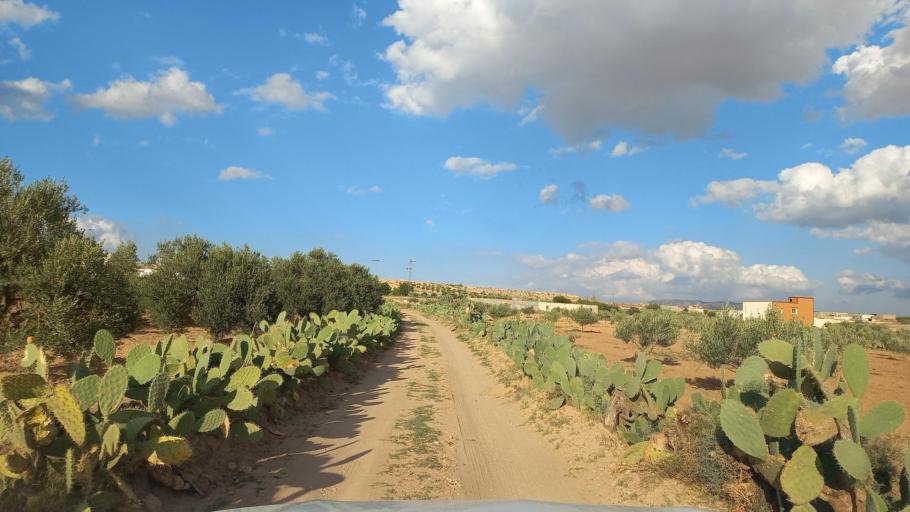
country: TN
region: Al Qasrayn
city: Sbiba
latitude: 35.3845
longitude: 9.0559
